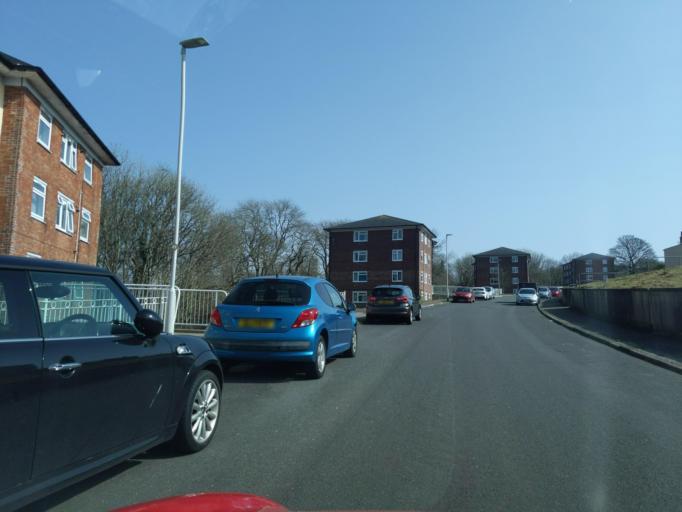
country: GB
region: England
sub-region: Plymouth
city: Plymouth
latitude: 50.4316
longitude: -4.1318
